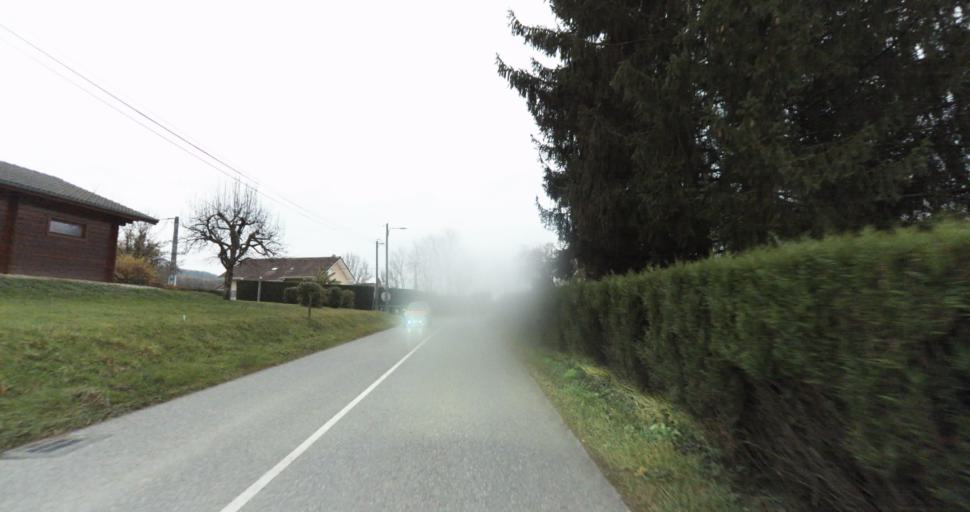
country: FR
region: Rhone-Alpes
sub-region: Departement de la Haute-Savoie
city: Saint-Felix
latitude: 45.8192
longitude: 5.9748
